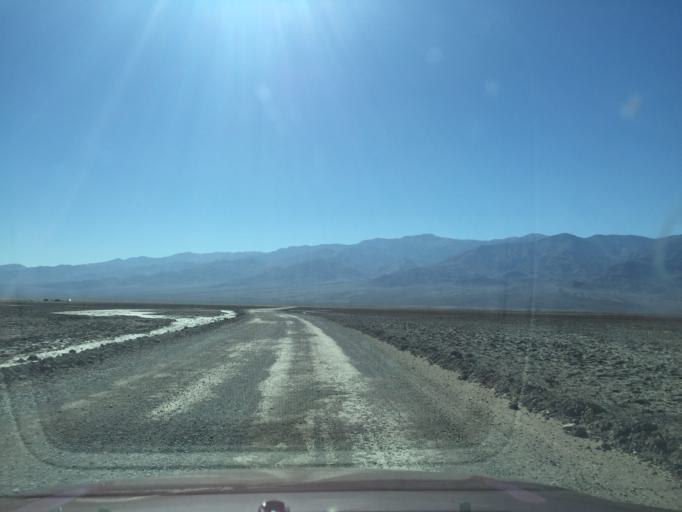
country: US
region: Nevada
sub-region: Nye County
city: Beatty
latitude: 36.2906
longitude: -116.8232
